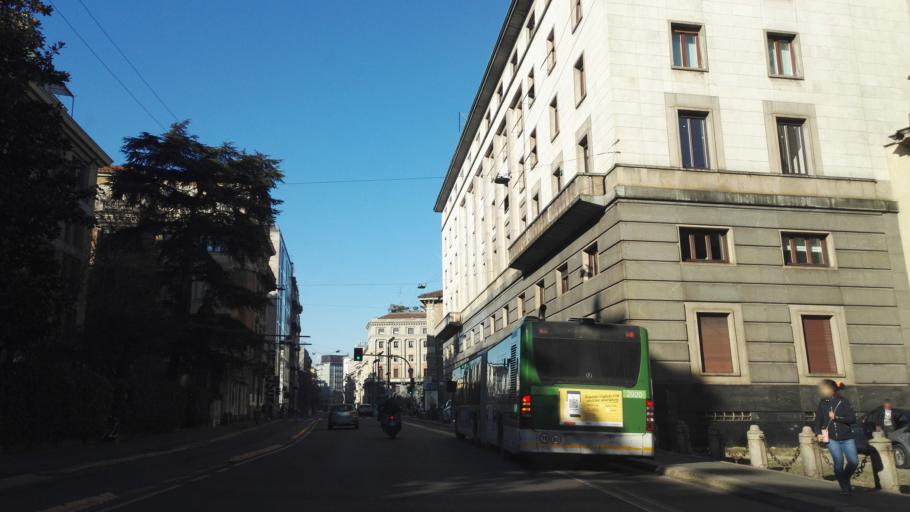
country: IT
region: Lombardy
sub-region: Citta metropolitana di Milano
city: Milano
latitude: 45.4692
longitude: 9.1990
